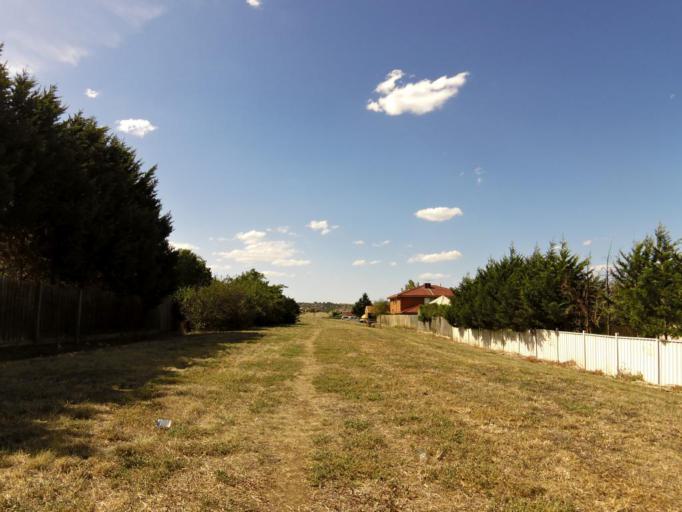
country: AU
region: Victoria
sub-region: Hume
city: Meadow Heights
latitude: -37.6575
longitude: 144.9038
